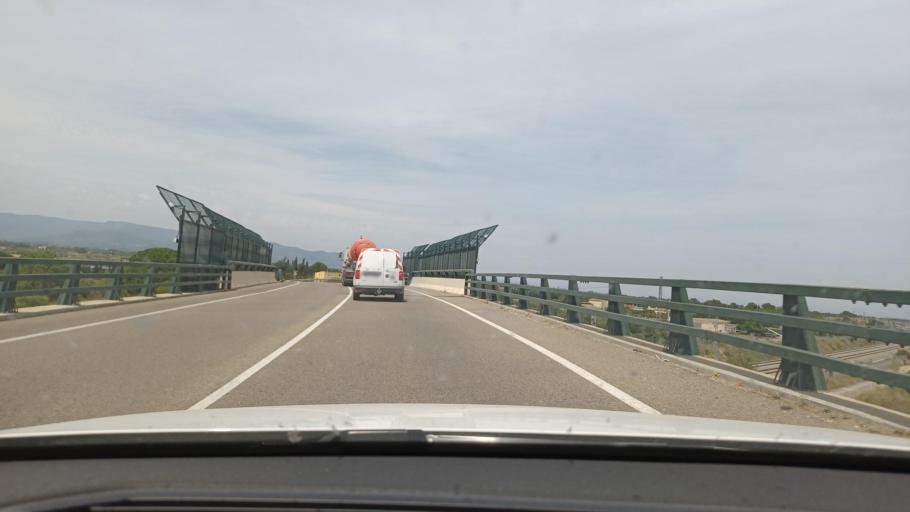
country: ES
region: Catalonia
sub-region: Provincia de Tarragona
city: Cambrils
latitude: 41.0931
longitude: 1.0829
